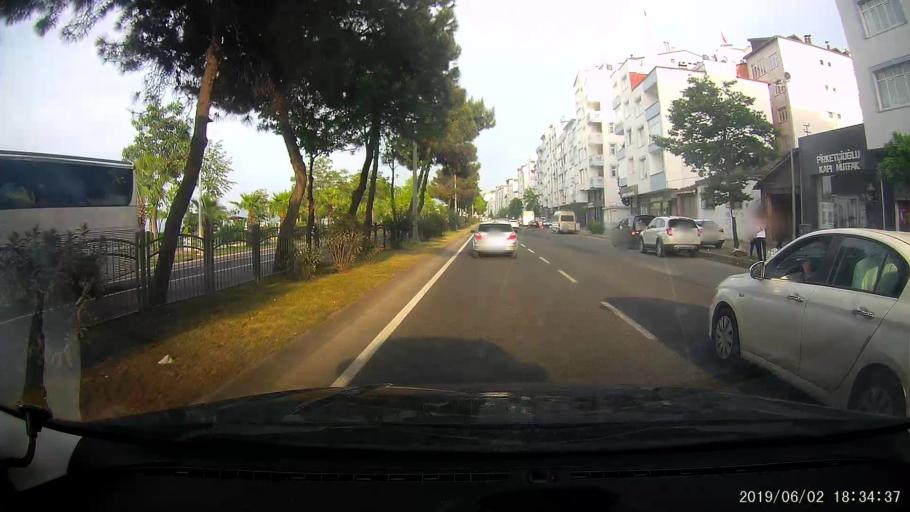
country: TR
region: Ordu
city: Fatsa
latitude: 41.0287
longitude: 37.5063
